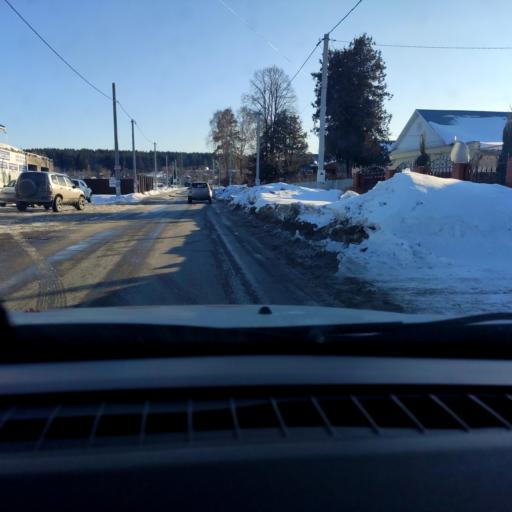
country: RU
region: Samara
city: Kurumoch
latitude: 53.4854
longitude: 50.0340
